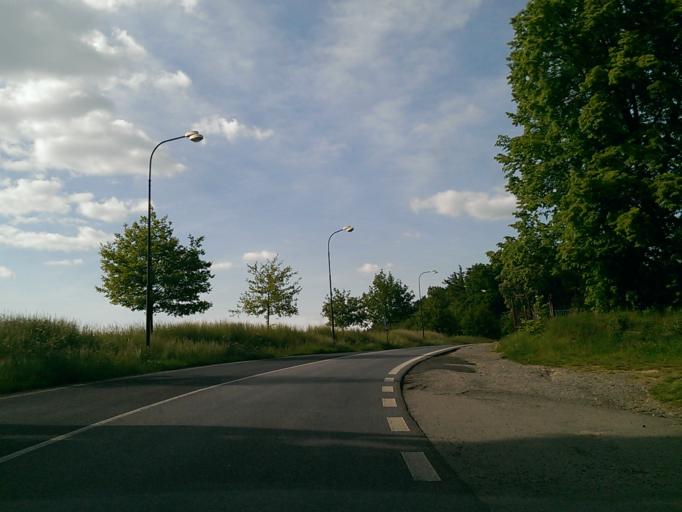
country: CZ
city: Duba
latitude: 50.5436
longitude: 14.5437
